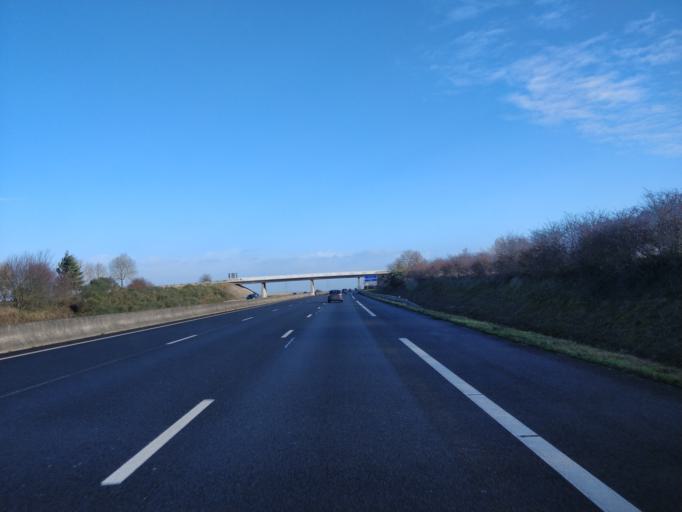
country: FR
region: Centre
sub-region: Departement du Loiret
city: Beaugency
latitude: 47.8104
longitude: 1.6256
